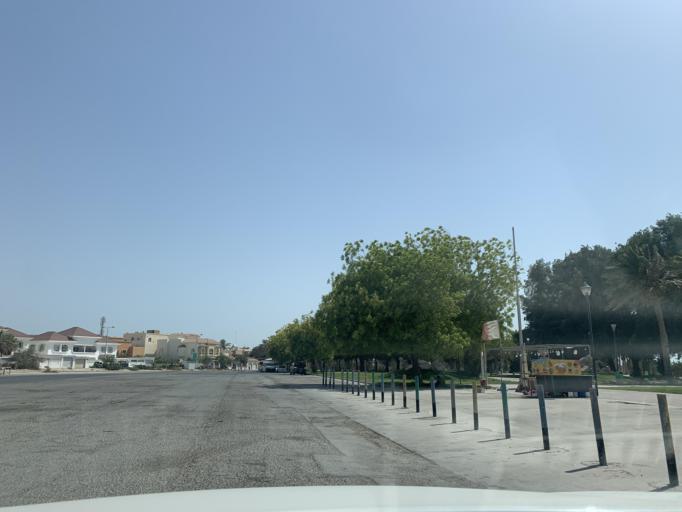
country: BH
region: Manama
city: Jidd Hafs
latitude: 26.2247
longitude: 50.4610
